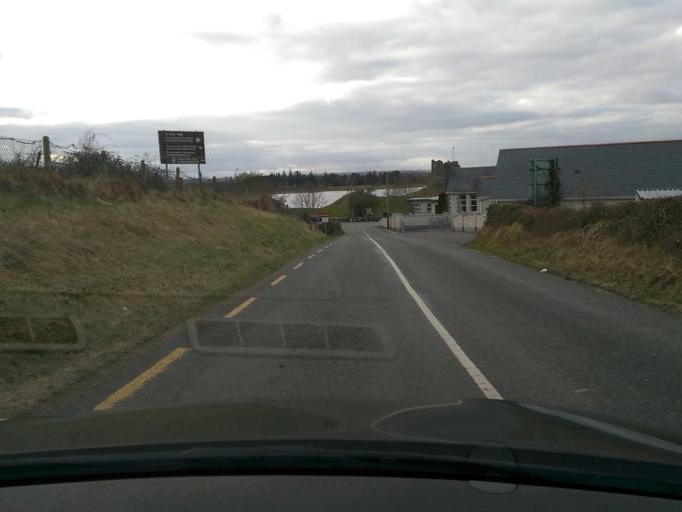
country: IE
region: Leinster
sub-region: An Iarmhi
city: Athlone
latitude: 53.3237
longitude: -7.9872
